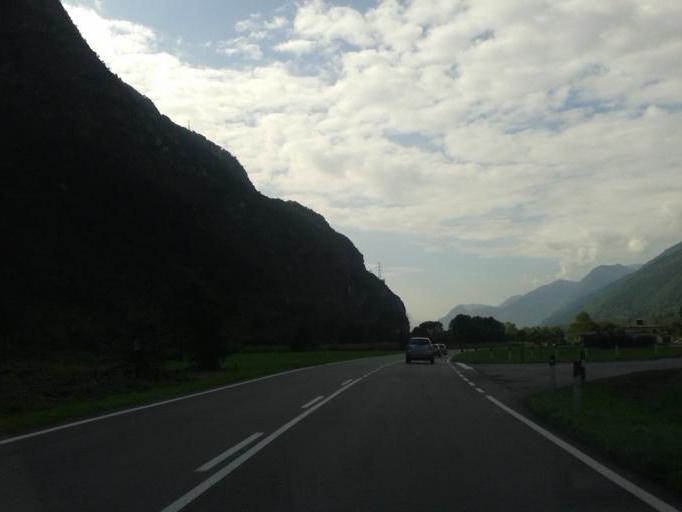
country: IT
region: Trentino-Alto Adige
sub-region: Provincia di Trento
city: Condino
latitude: 45.8710
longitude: 10.5859
